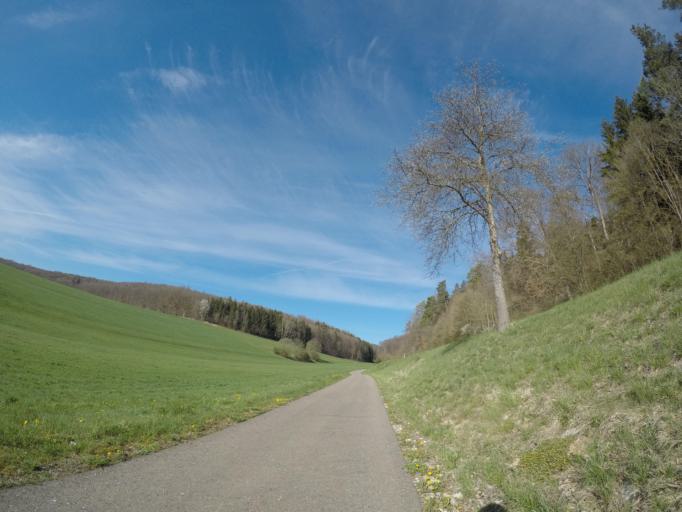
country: DE
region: Baden-Wuerttemberg
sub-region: Tuebingen Region
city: Allmendingen
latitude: 48.3477
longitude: 9.6838
